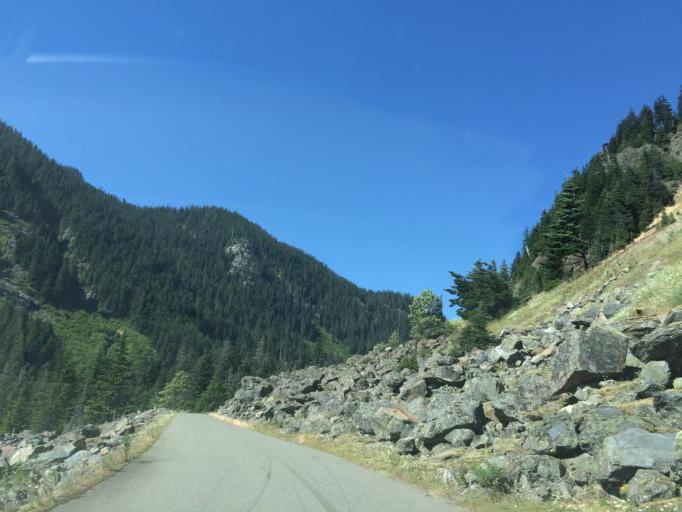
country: US
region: Washington
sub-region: King County
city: Tanner
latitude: 47.4206
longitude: -121.4334
